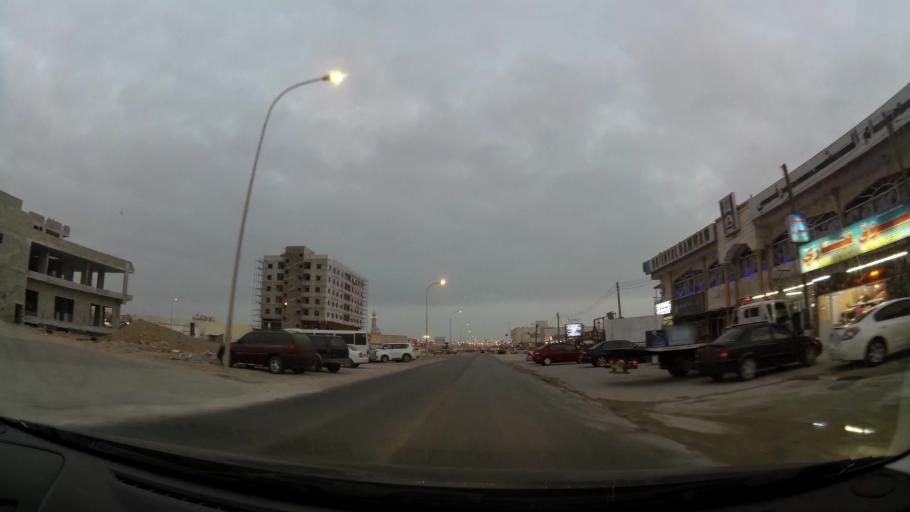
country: OM
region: Zufar
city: Salalah
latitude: 17.0247
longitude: 54.0546
